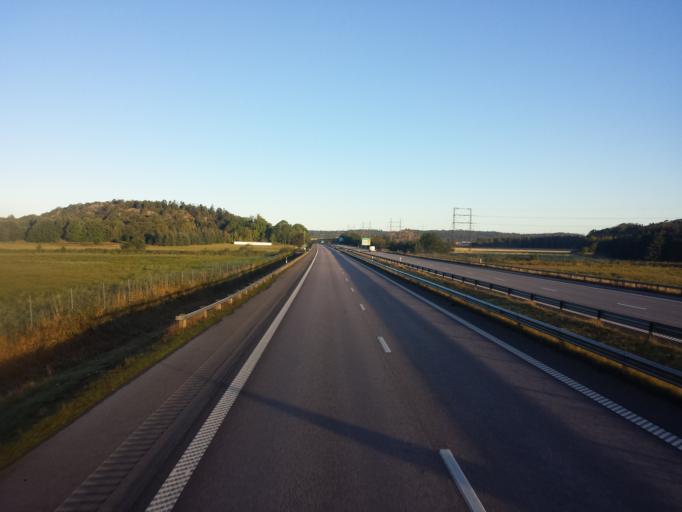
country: SE
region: Halland
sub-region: Kungsbacka Kommun
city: Kungsbacka
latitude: 57.4584
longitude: 12.0840
